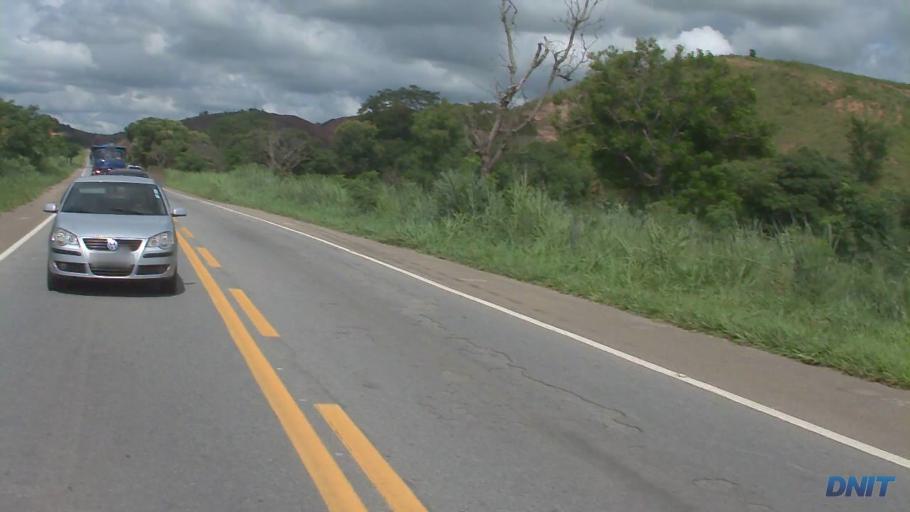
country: BR
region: Minas Gerais
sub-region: Belo Oriente
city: Belo Oriente
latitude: -19.1403
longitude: -42.2219
